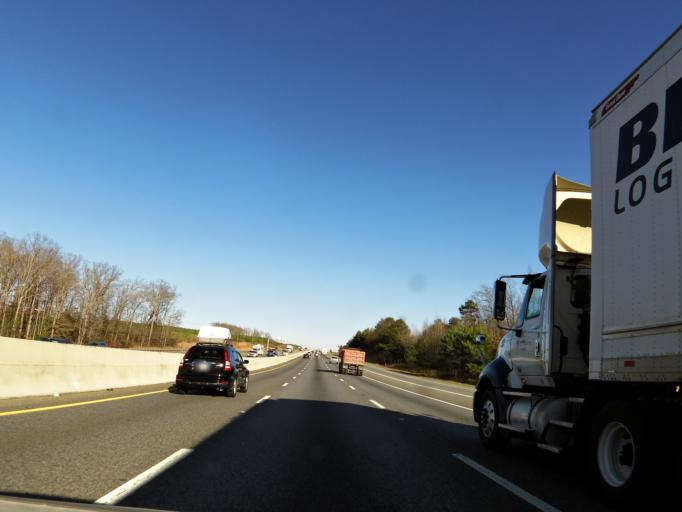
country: US
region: South Carolina
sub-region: Greenville County
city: Greer
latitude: 34.8781
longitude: -82.2106
